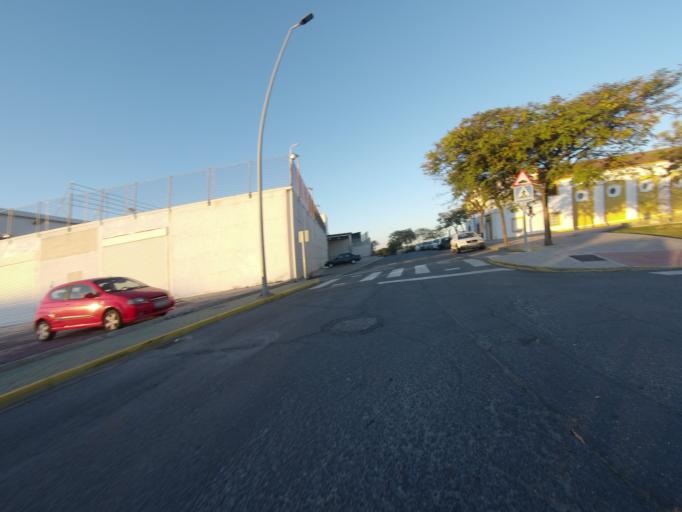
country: ES
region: Andalusia
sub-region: Provincia de Huelva
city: Aljaraque
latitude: 37.2745
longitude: -6.9894
